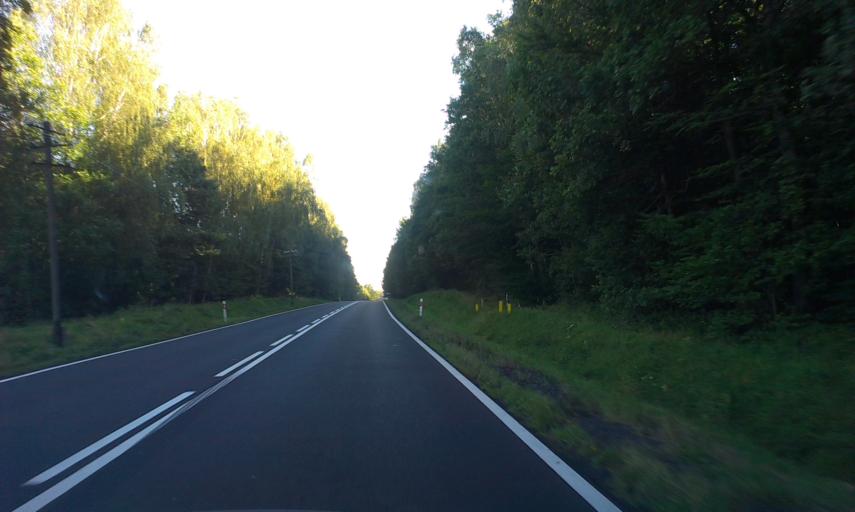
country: PL
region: West Pomeranian Voivodeship
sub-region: Powiat szczecinecki
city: Szczecinek
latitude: 53.8235
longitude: 16.6398
